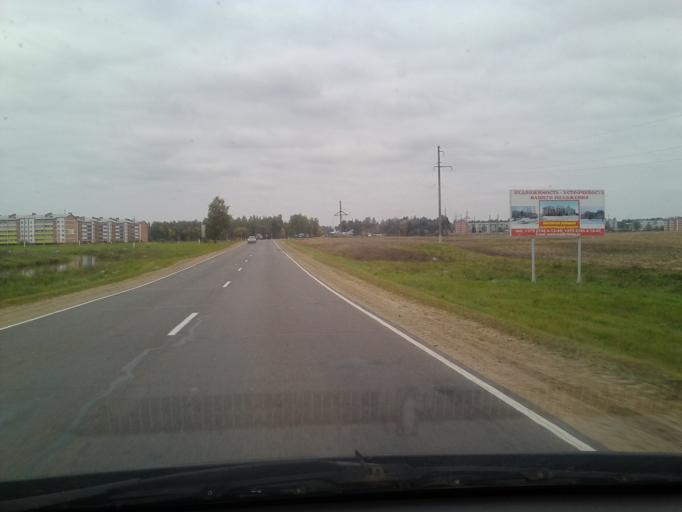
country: BY
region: Vitebsk
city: Pastavy
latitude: 55.1051
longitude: 26.8743
